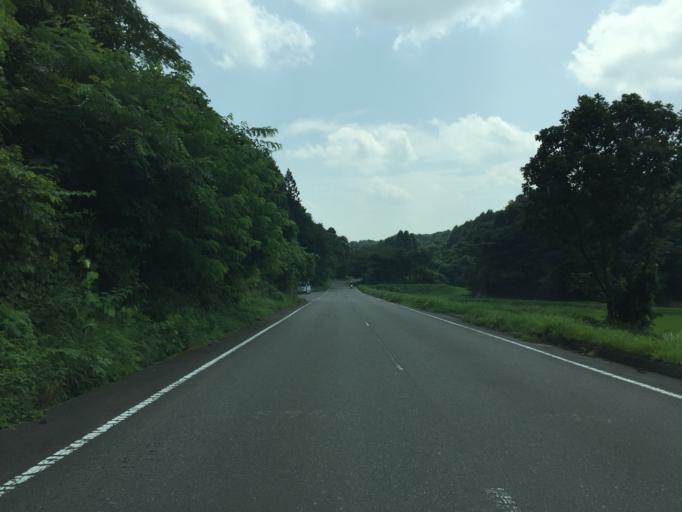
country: JP
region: Fukushima
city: Ishikawa
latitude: 37.2248
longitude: 140.5570
